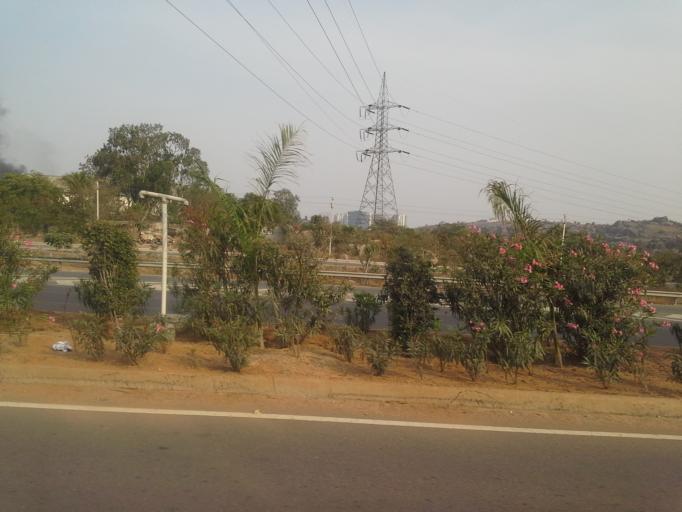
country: IN
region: Telangana
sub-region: Rangareddi
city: Kukatpalli
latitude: 17.4156
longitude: 78.3555
